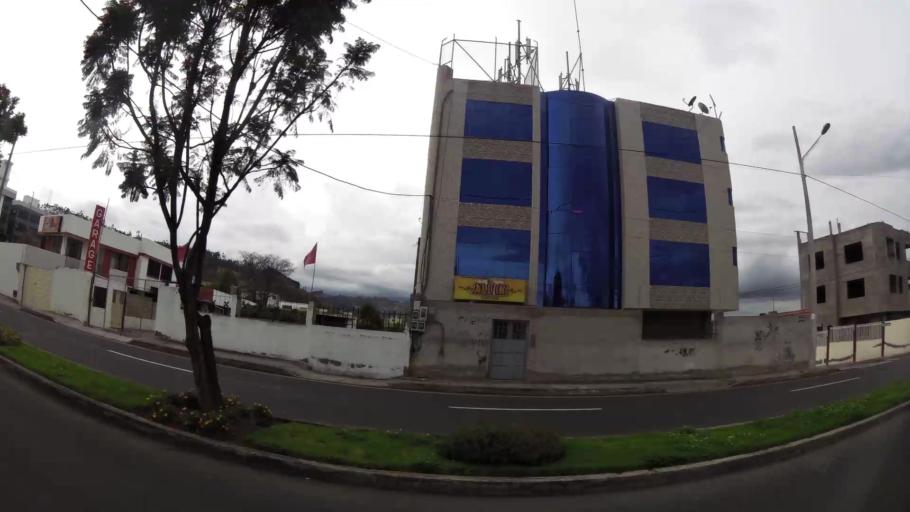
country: EC
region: Tungurahua
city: Ambato
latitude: -1.2748
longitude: -78.6368
